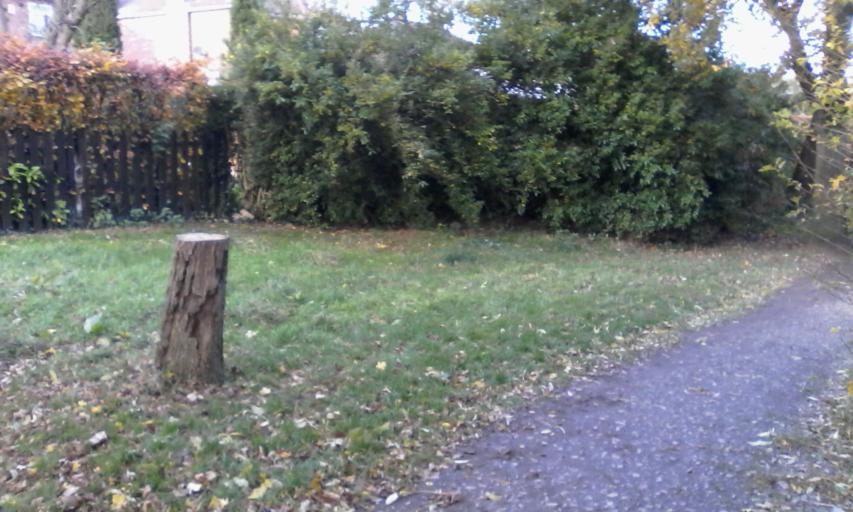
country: GB
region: England
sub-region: Nottinghamshire
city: Arnold
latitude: 52.9865
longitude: -1.1142
